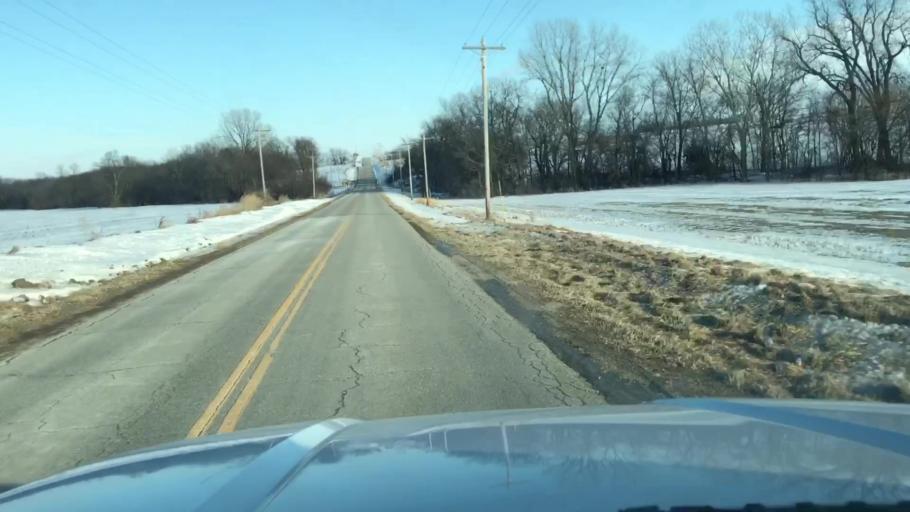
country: US
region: Missouri
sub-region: Andrew County
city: Savannah
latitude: 40.0246
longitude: -94.9064
